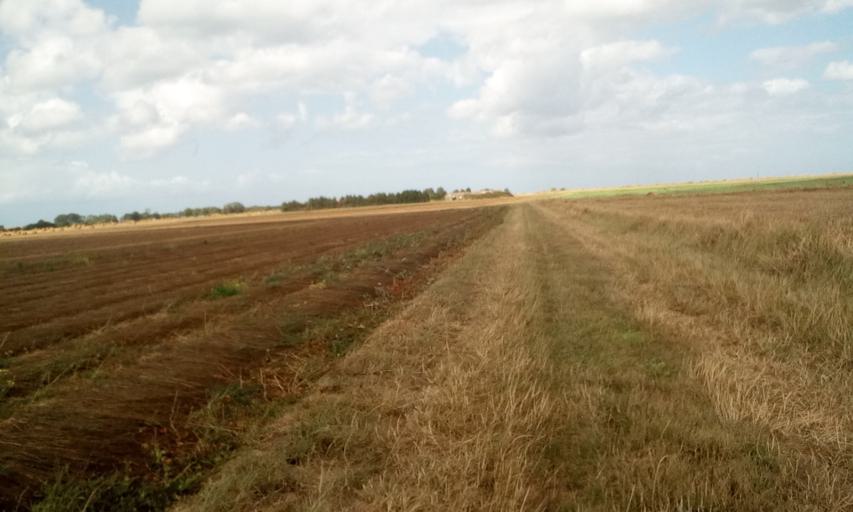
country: FR
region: Lower Normandy
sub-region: Departement du Calvados
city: Ver-sur-Mer
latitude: 49.3196
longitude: -0.5293
